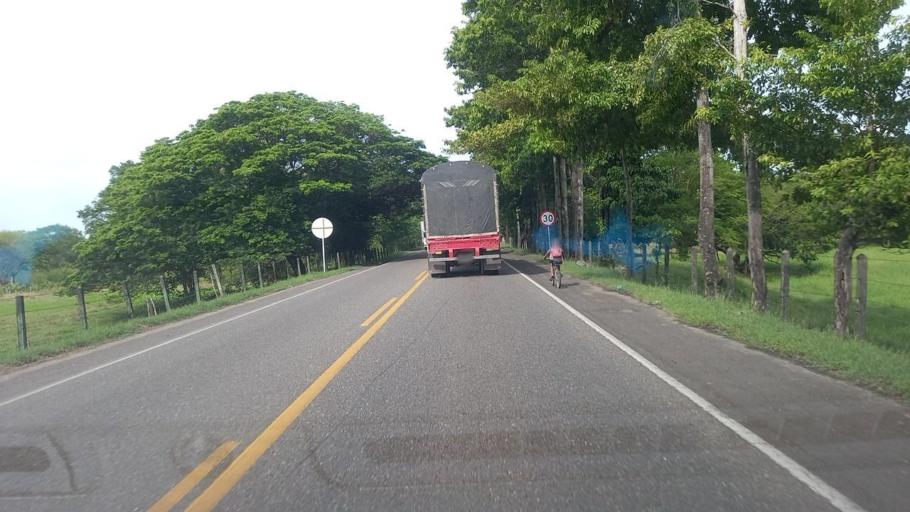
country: CO
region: Antioquia
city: Puerto Berrio
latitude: 6.3265
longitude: -74.4375
